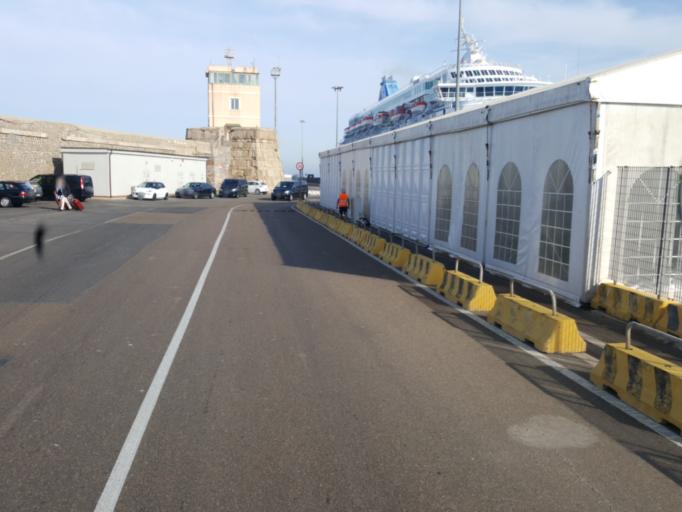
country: IT
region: Latium
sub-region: Citta metropolitana di Roma Capitale
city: Civitavecchia
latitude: 42.0898
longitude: 11.7860
